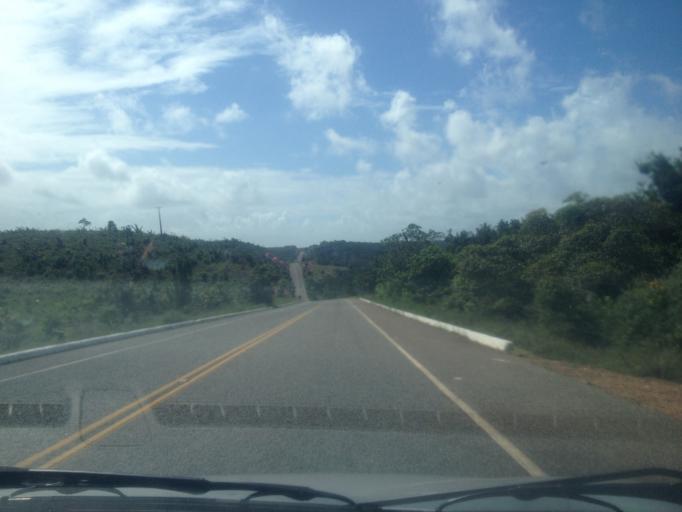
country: BR
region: Bahia
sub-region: Conde
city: Conde
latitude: -11.9268
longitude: -37.6690
